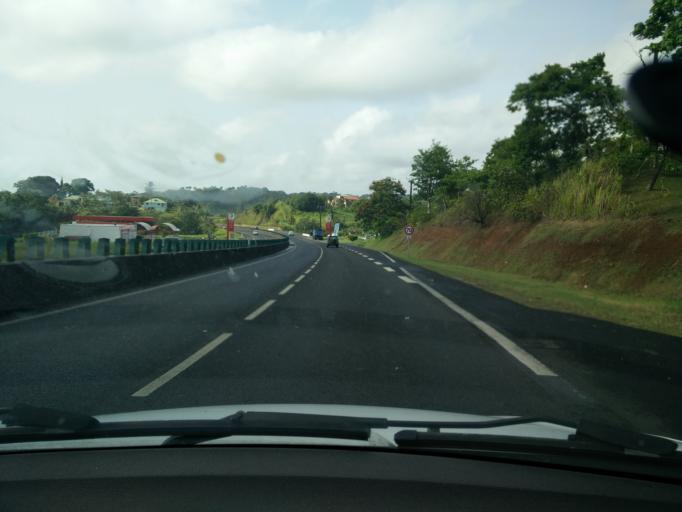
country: GP
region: Guadeloupe
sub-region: Guadeloupe
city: Petit-Bourg
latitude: 16.1889
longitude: -61.6077
